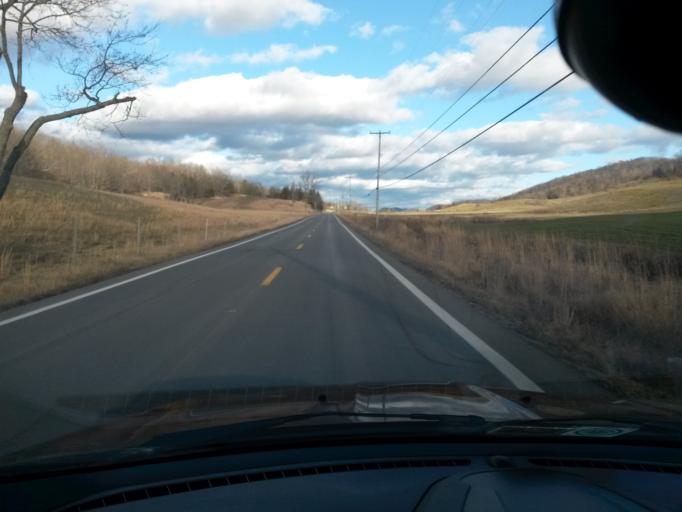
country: US
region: Virginia
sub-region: Giles County
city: Pearisburg
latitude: 37.4220
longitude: -80.7348
